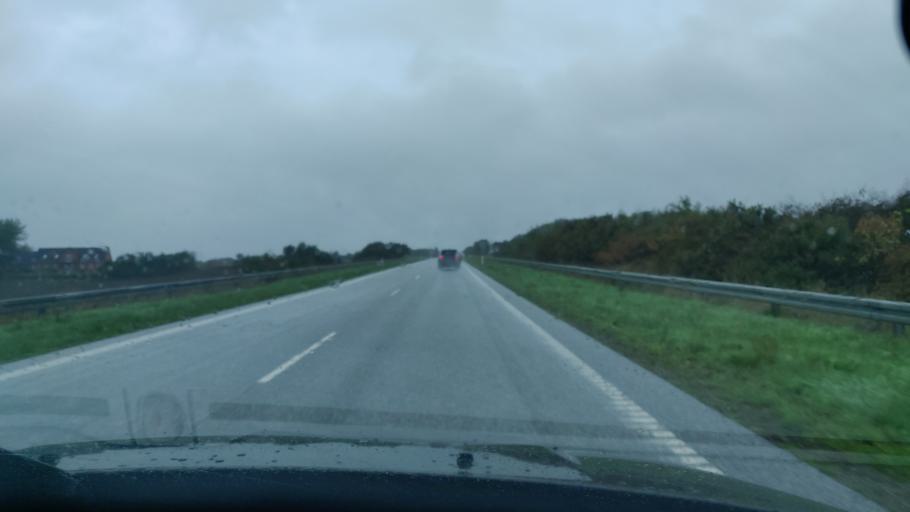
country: DK
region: North Denmark
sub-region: Thisted Kommune
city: Hurup
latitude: 56.8140
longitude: 8.4866
